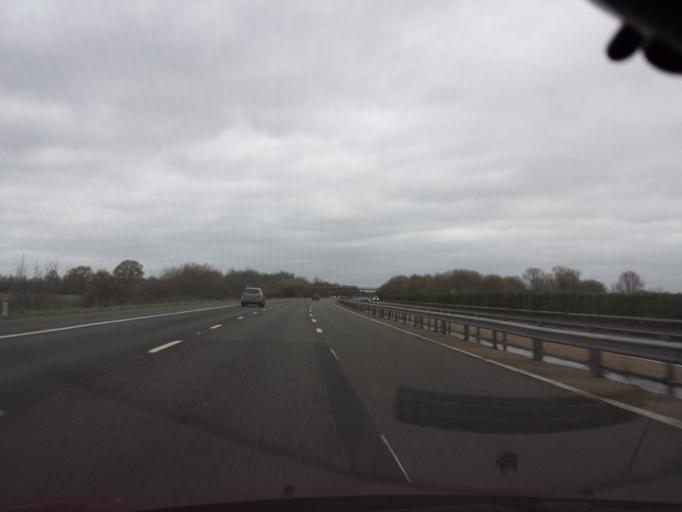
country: GB
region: England
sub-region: Surrey
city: Shepperton
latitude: 51.4005
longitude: -0.4510
